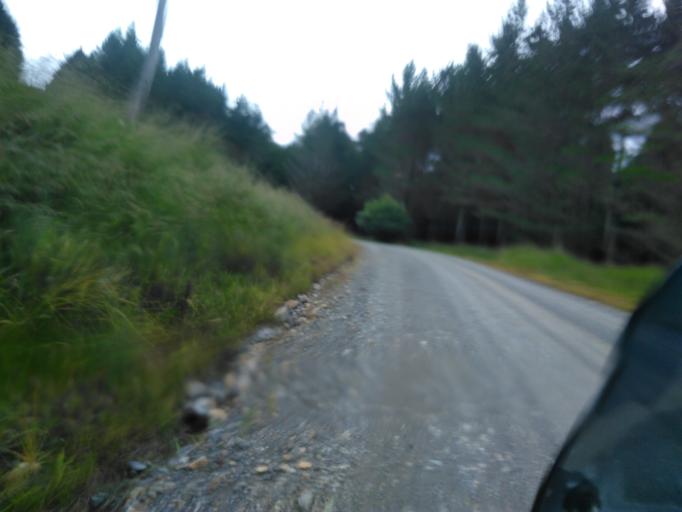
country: NZ
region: Gisborne
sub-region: Gisborne District
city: Gisborne
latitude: -38.0489
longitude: 178.1240
